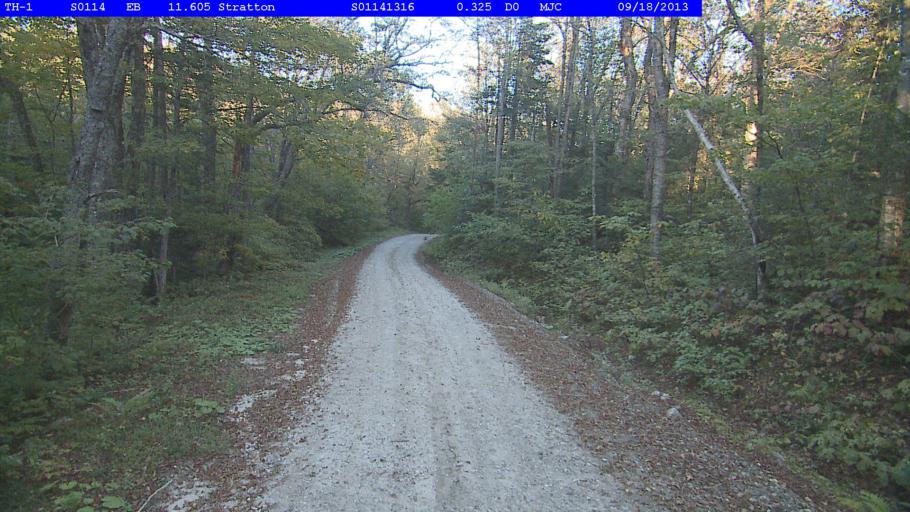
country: US
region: Vermont
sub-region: Bennington County
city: Manchester Center
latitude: 43.0623
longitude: -72.9951
